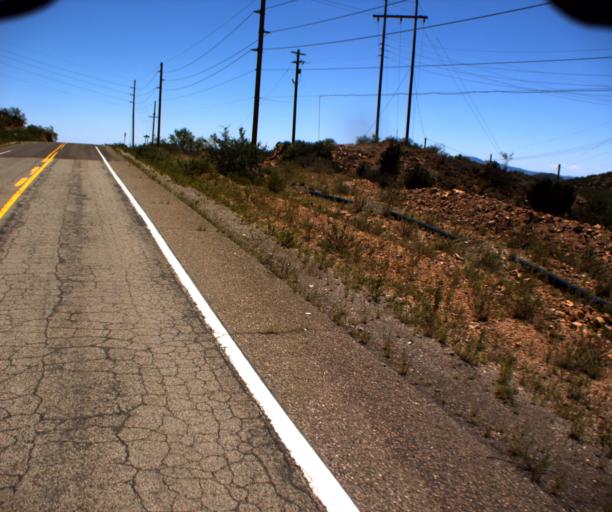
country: US
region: Arizona
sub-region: Greenlee County
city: Morenci
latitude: 33.0726
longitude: -109.3776
